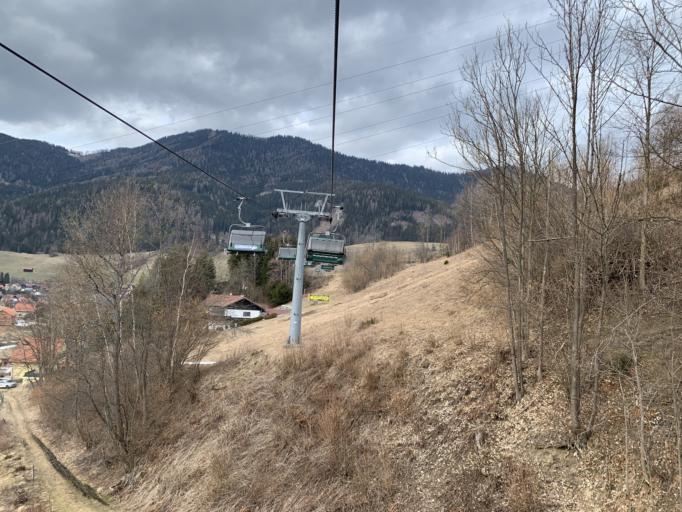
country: AT
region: Styria
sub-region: Politischer Bezirk Bruck-Muerzzuschlag
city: Spital am Semmering
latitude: 47.6100
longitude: 15.7590
